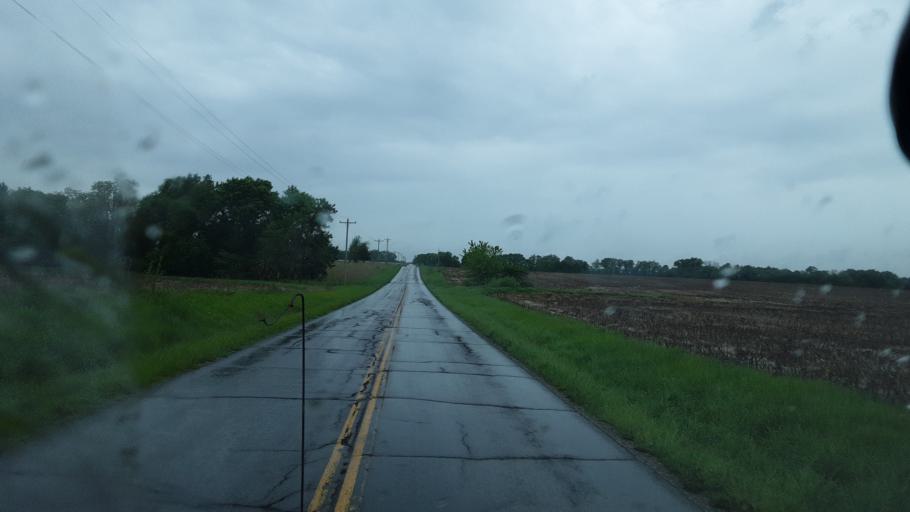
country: US
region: Missouri
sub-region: Randolph County
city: Moberly
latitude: 39.3928
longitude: -92.2389
